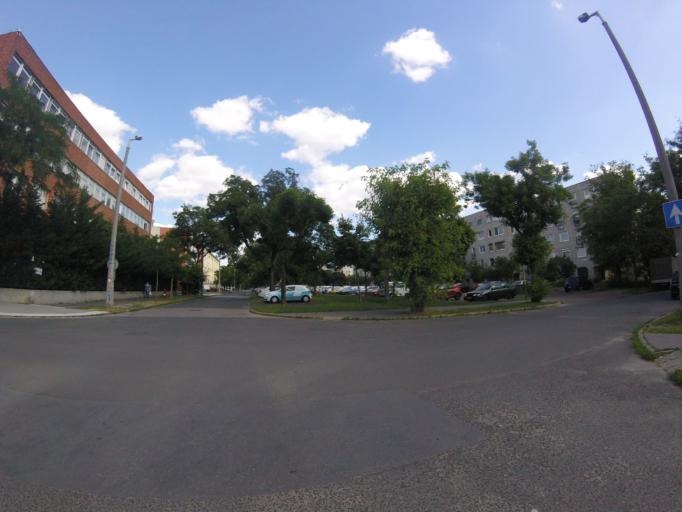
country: HU
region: Budapest
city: Budapest XIII. keruelet
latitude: 47.5406
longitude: 19.0888
